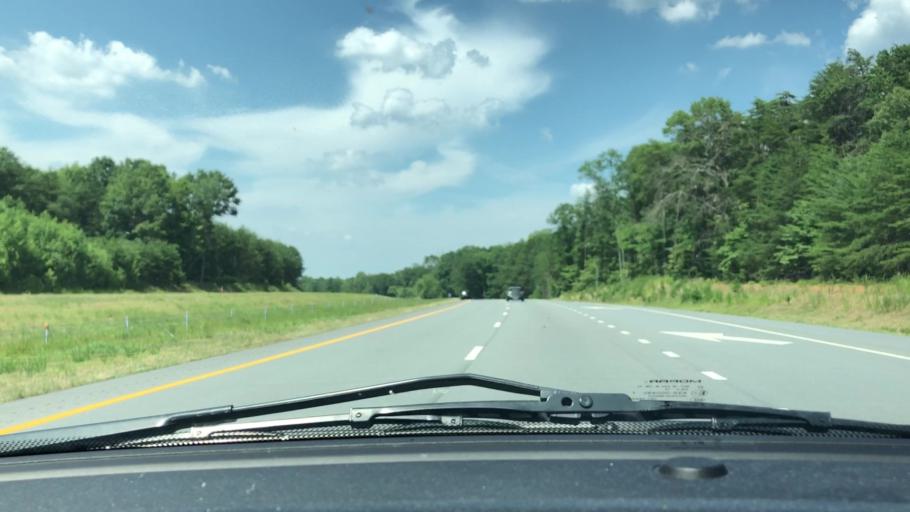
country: US
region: North Carolina
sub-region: Guilford County
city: Oak Ridge
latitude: 36.1408
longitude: -79.9599
